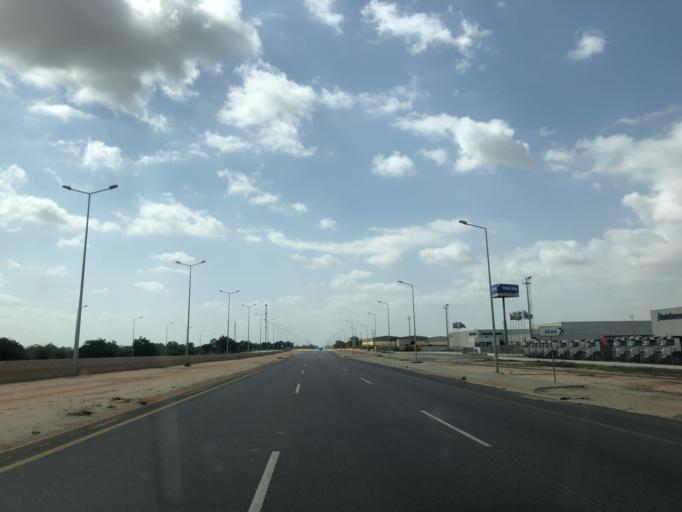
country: AO
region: Luanda
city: Luanda
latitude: -8.9899
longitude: 13.5040
